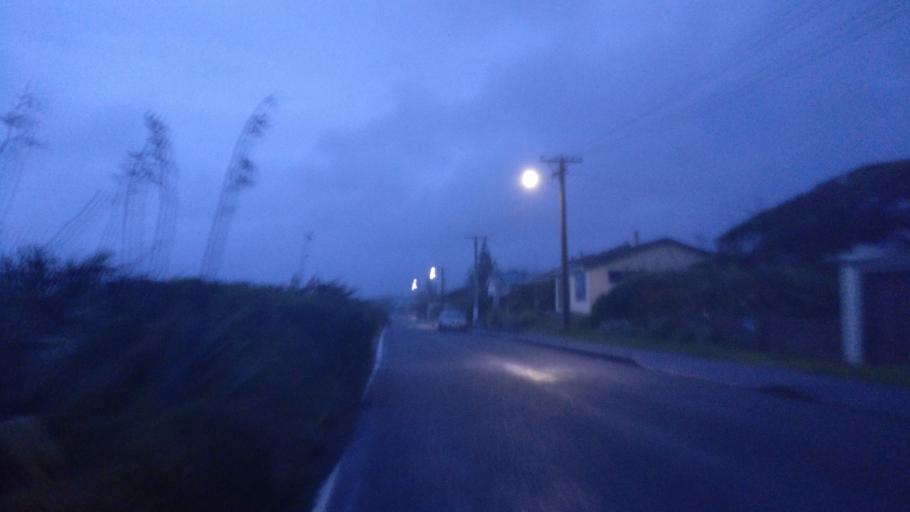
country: NZ
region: Wellington
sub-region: Kapiti Coast District
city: Paraparaumu
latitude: -40.9770
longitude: 174.9572
